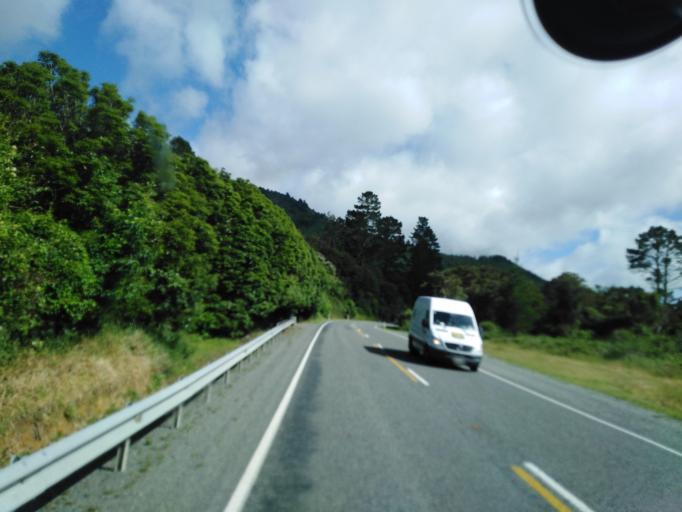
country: NZ
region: Nelson
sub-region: Nelson City
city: Nelson
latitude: -41.2912
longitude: 173.5726
